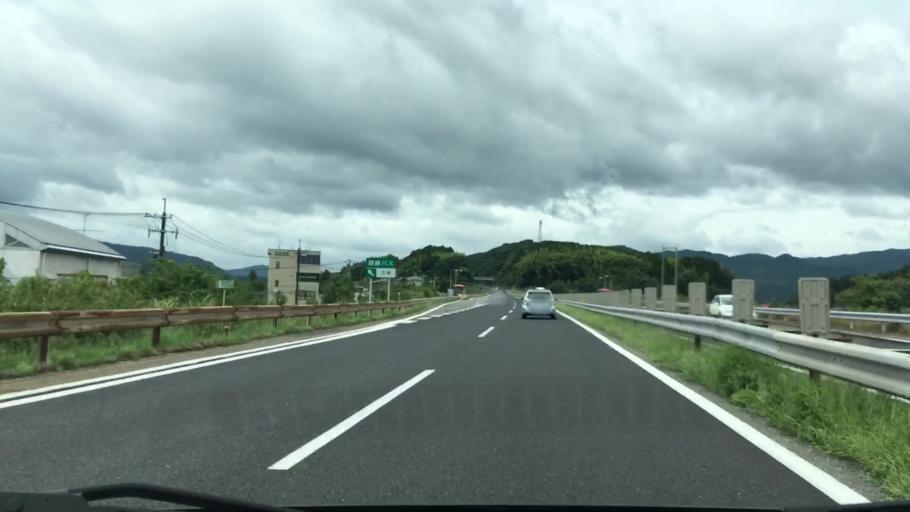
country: JP
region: Okayama
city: Tsuyama
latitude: 35.0623
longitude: 133.8999
